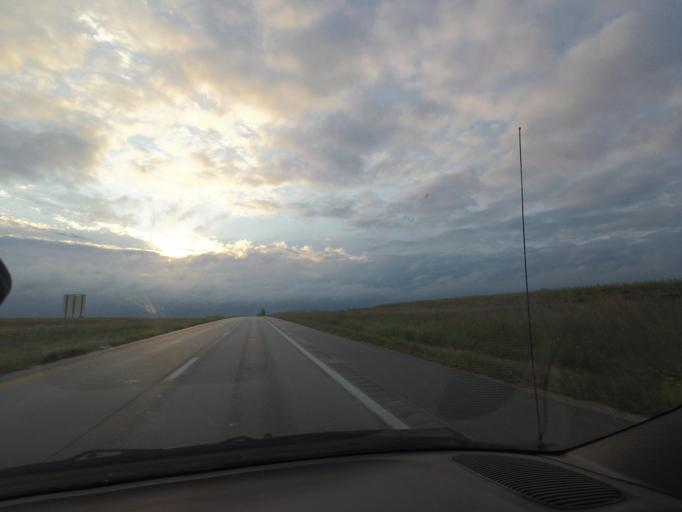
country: US
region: Missouri
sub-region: Shelby County
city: Shelbina
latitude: 39.6883
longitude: -92.0172
